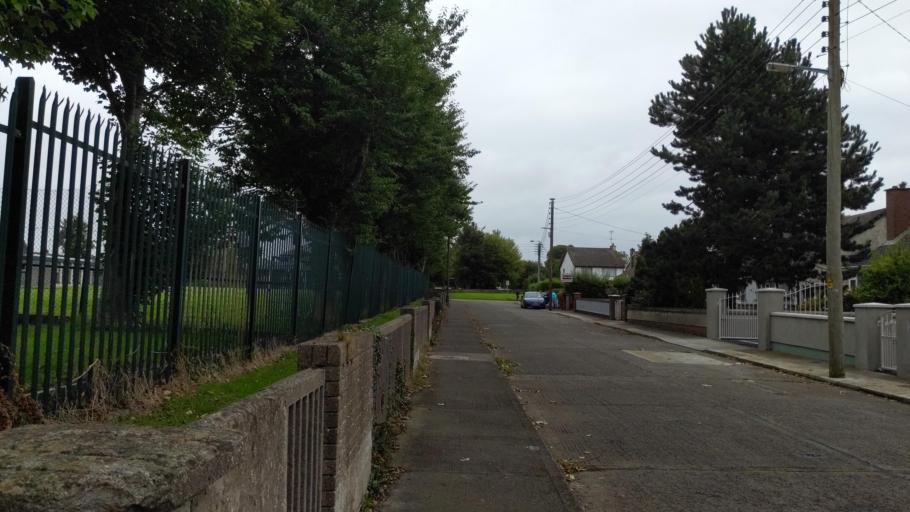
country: IE
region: Leinster
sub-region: Lu
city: Drogheda
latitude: 53.7110
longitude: -6.3589
